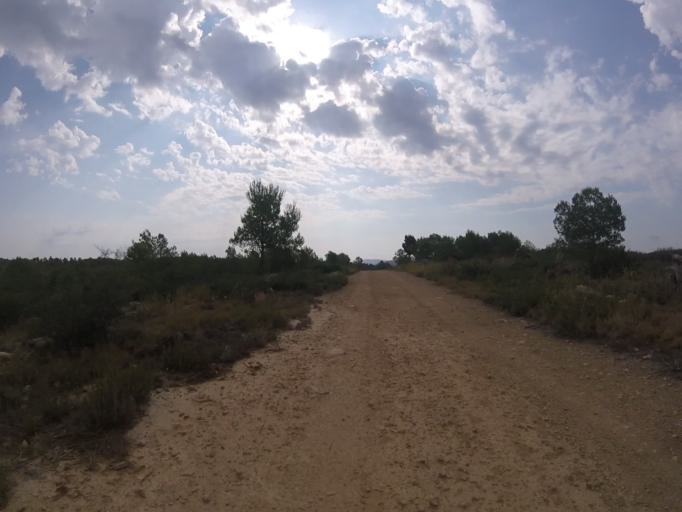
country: ES
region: Valencia
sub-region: Provincia de Castello
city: Alcala de Xivert
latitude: 40.3789
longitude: 0.2082
